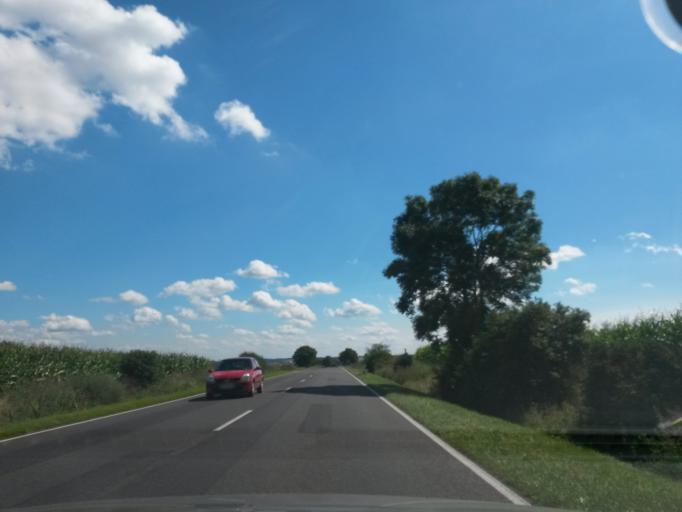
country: DE
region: Brandenburg
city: Meyenburg
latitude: 53.0282
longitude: 14.1930
